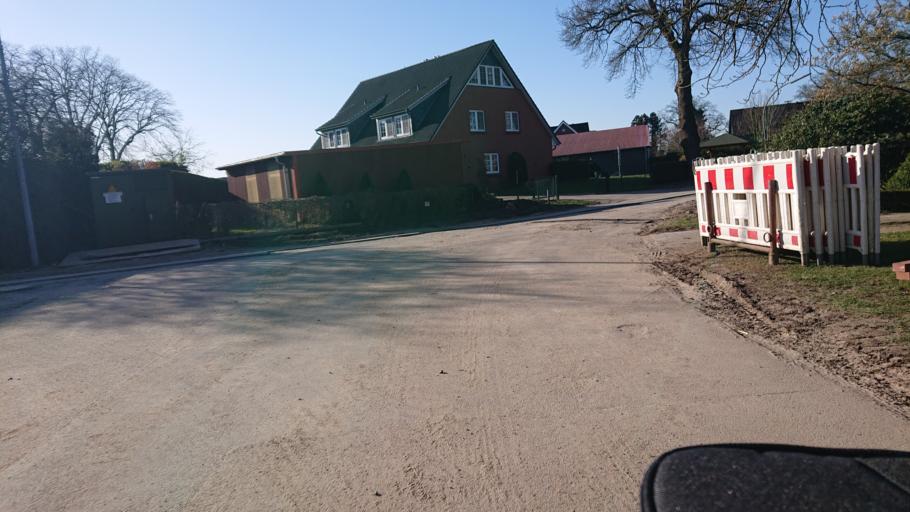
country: DE
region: Schleswig-Holstein
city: Hasloh
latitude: 53.6777
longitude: 9.9001
